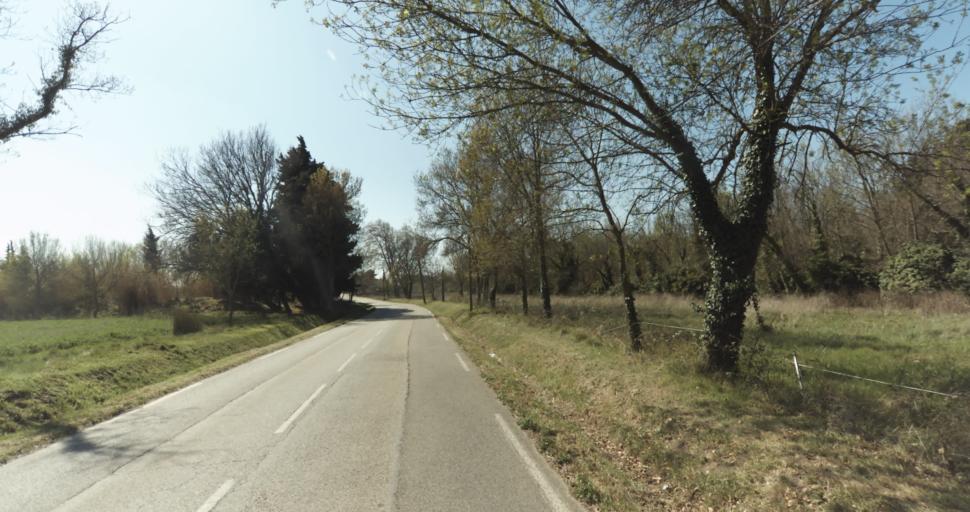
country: FR
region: Provence-Alpes-Cote d'Azur
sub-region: Departement des Bouches-du-Rhone
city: Pelissanne
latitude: 43.6258
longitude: 5.1352
